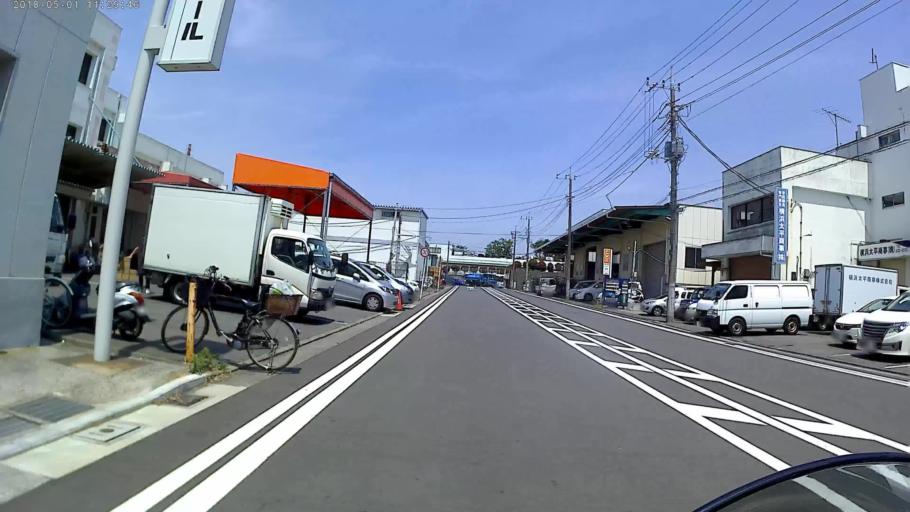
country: JP
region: Kanagawa
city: Minami-rinkan
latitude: 35.4995
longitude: 139.4870
